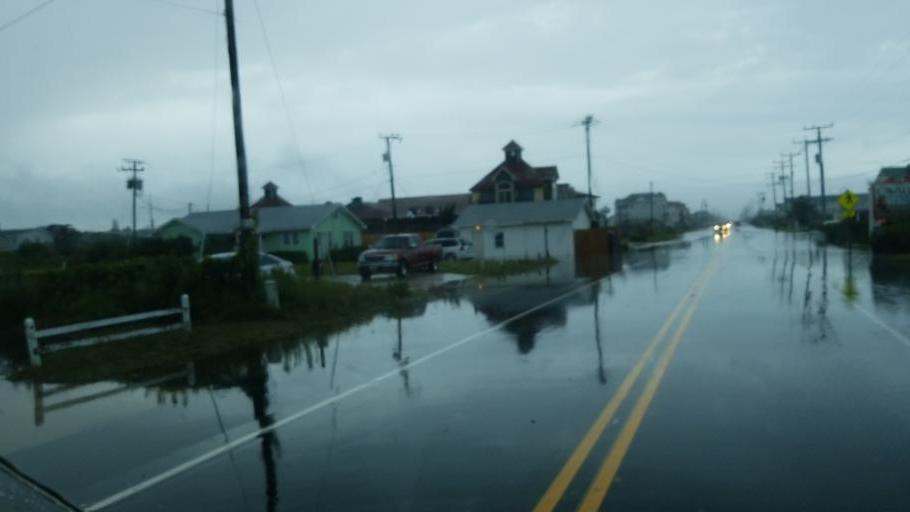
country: US
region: North Carolina
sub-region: Dare County
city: Kill Devil Hills
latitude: 36.0110
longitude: -75.6555
